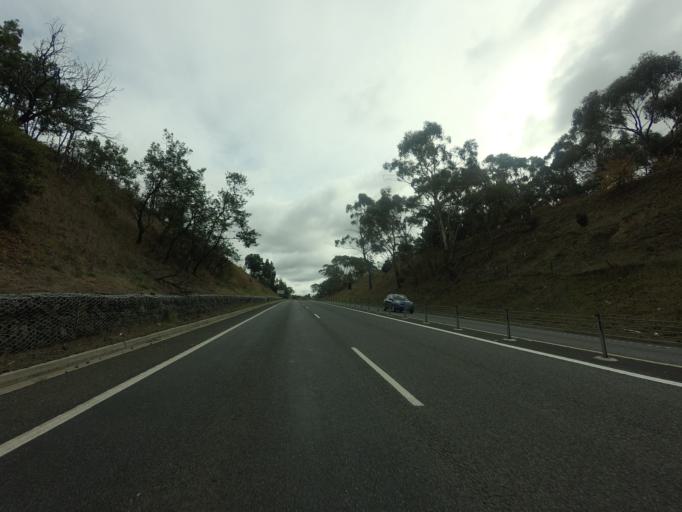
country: AU
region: Tasmania
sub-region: Brighton
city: Bridgewater
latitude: -42.5769
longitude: 147.2249
